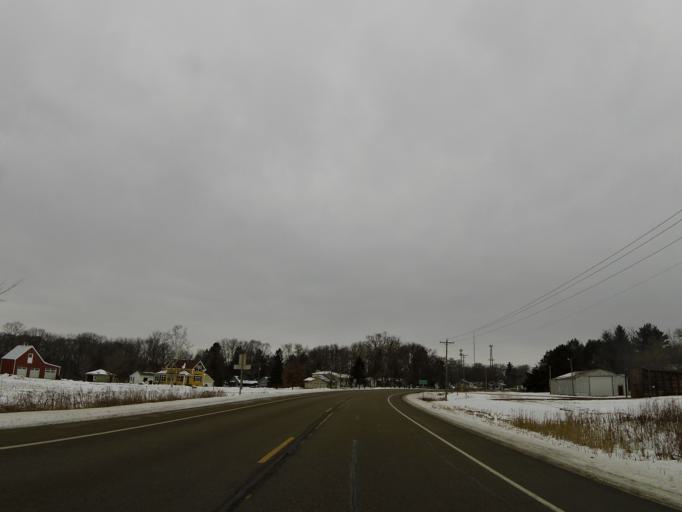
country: US
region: Minnesota
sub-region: Washington County
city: Stillwater
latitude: 45.0556
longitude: -92.7904
